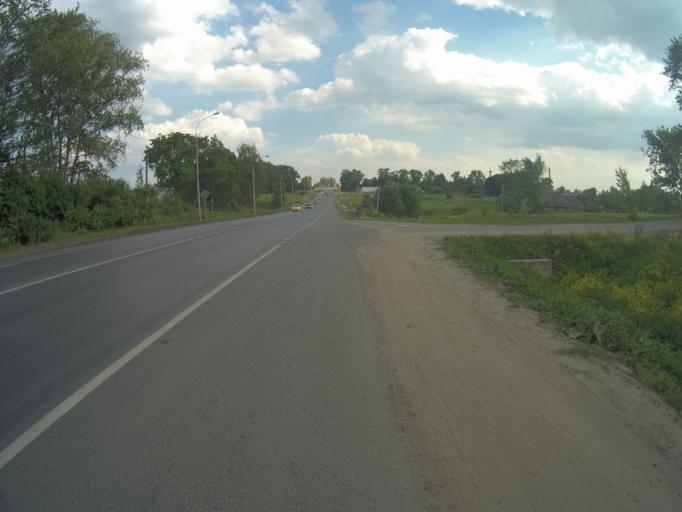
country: RU
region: Vladimir
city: Suzdal'
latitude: 56.3219
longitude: 40.4726
